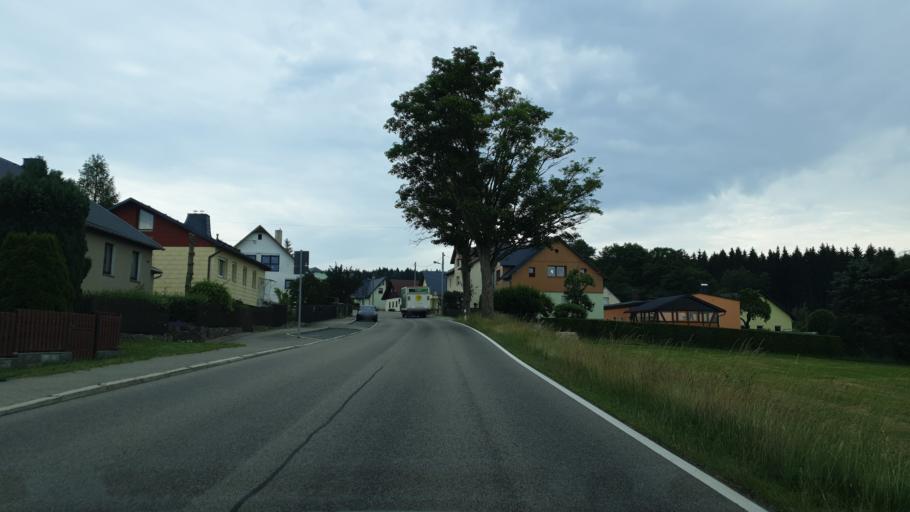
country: DE
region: Saxony
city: Auerbach
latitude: 50.4890
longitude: 12.4304
